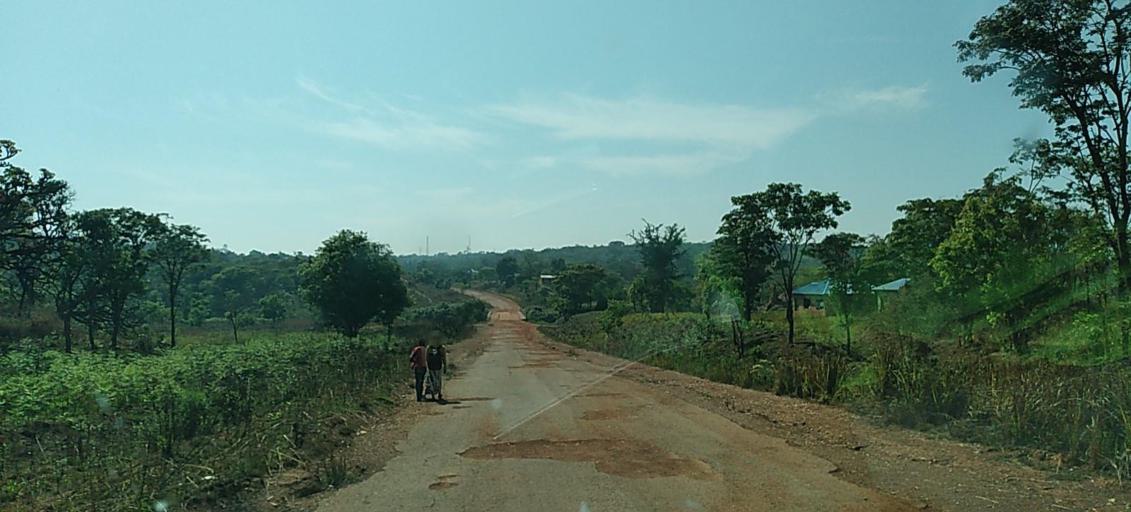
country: ZM
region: North-Western
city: Mwinilunga
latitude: -11.8248
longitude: 25.1238
